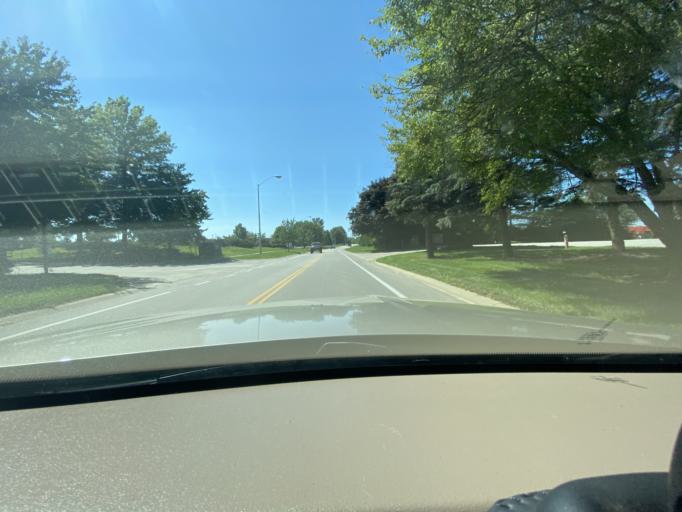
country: US
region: Indiana
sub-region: Monroe County
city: Bloomington
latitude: 39.1507
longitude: -86.5769
